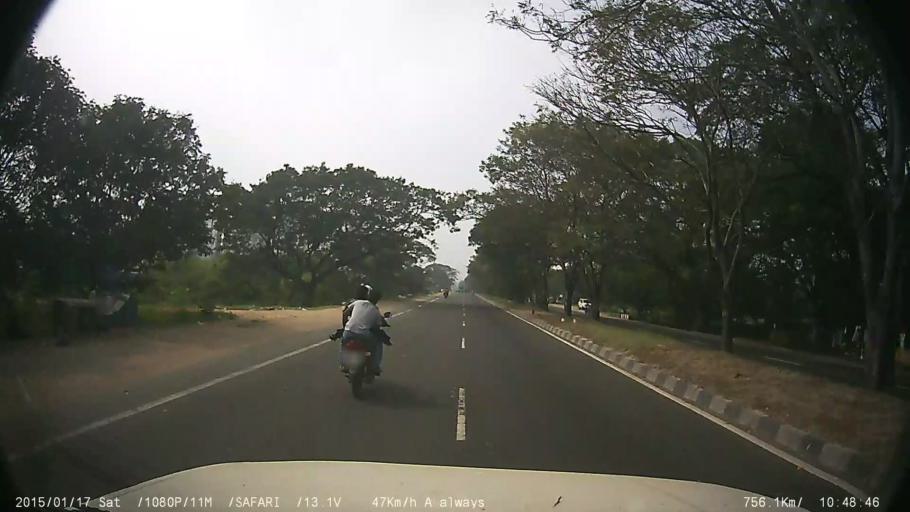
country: IN
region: Tamil Nadu
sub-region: Kancheepuram
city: Guduvancheri
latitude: 12.8561
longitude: 80.0695
